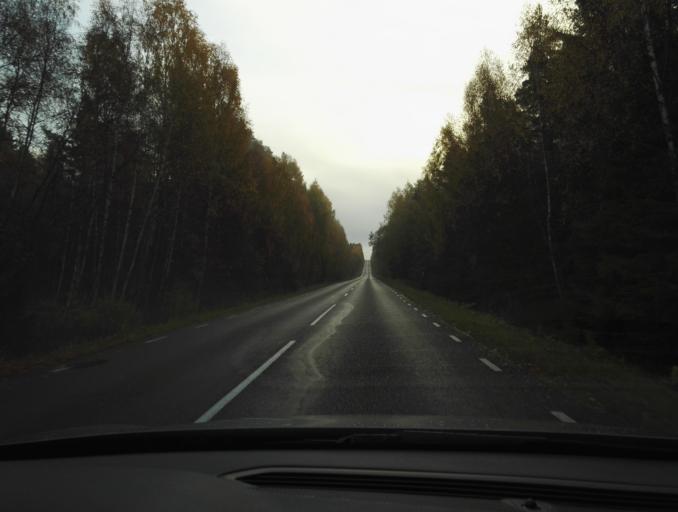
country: SE
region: Kronoberg
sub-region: Alvesta Kommun
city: Moheda
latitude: 57.0110
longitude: 14.7071
